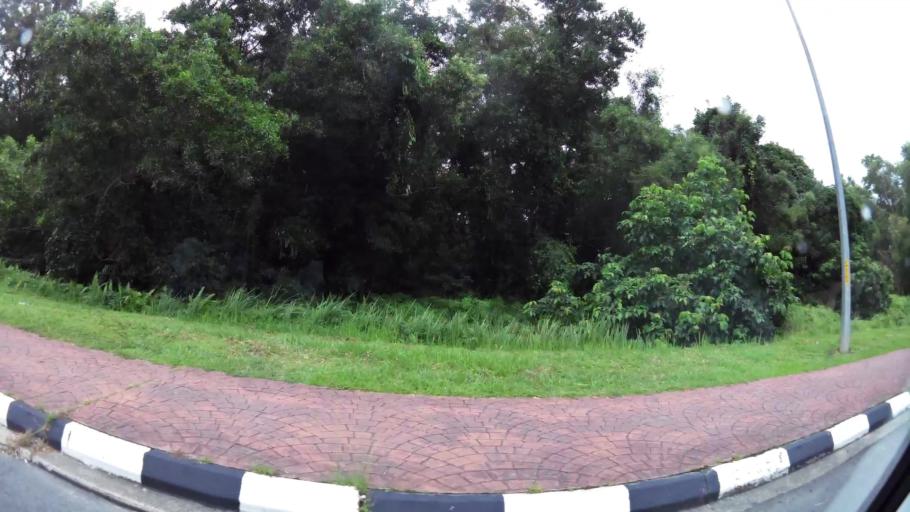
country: BN
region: Brunei and Muara
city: Bandar Seri Begawan
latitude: 4.9008
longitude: 114.9241
